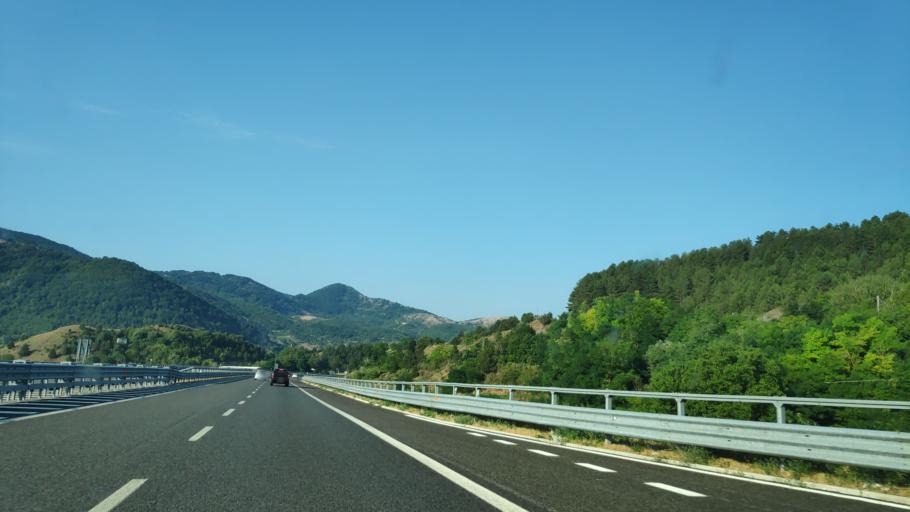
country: IT
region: Calabria
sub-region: Provincia di Cosenza
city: Mormanno
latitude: 39.8822
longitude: 16.0110
